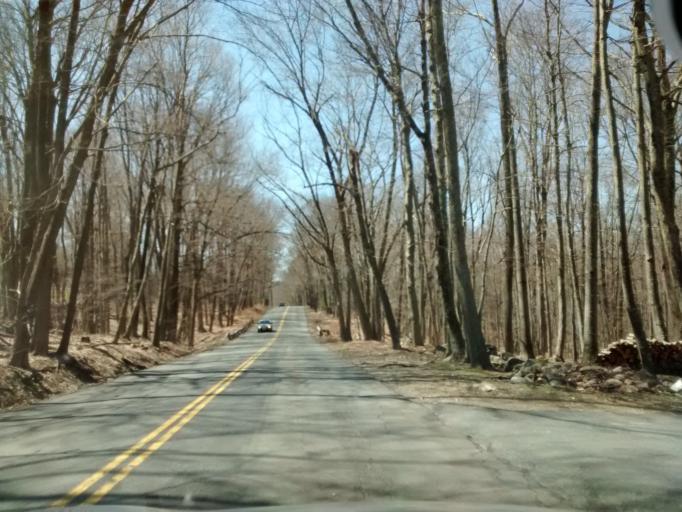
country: US
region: Massachusetts
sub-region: Worcester County
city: Sutton
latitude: 42.1339
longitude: -71.7567
